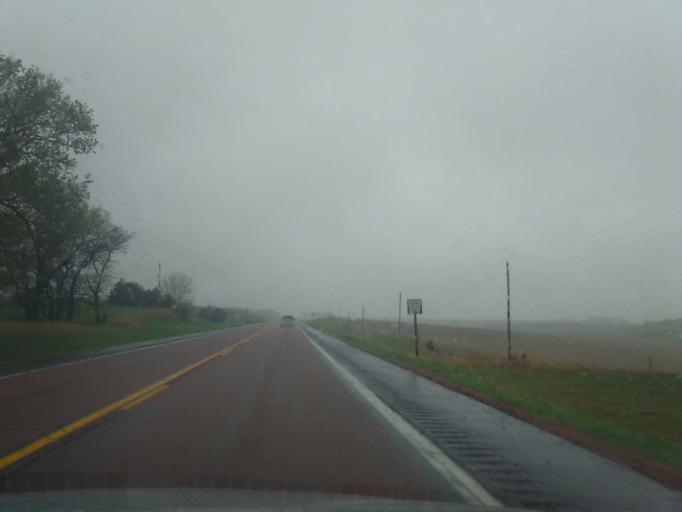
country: US
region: Nebraska
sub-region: Wayne County
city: Wayne
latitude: 42.2355
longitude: -97.1351
